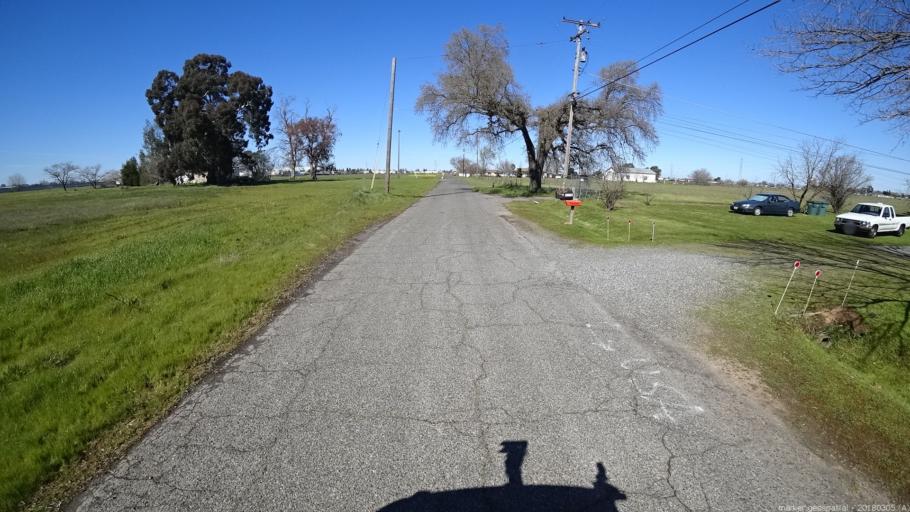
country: US
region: California
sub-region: Sacramento County
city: Florin
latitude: 38.5013
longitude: -121.3790
